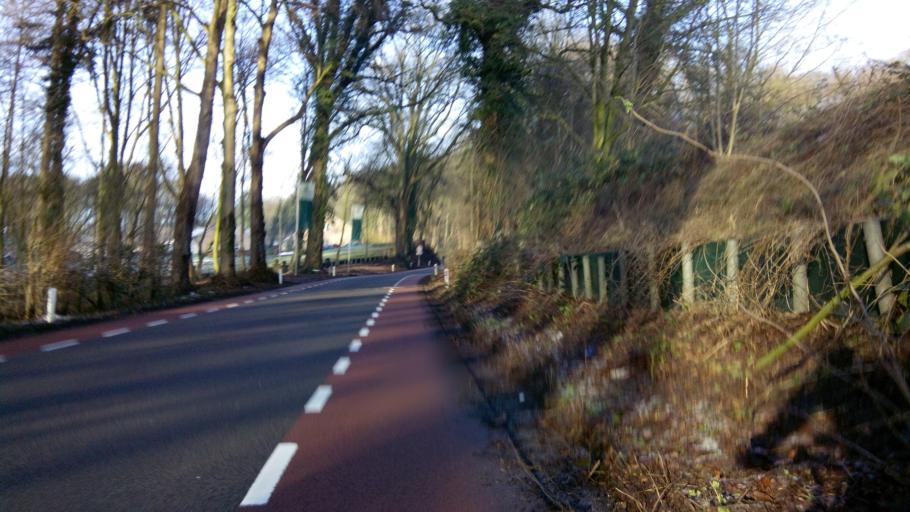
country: NL
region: Gelderland
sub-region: Gemeente Groesbeek
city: Berg en Dal
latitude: 51.8156
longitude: 5.9344
